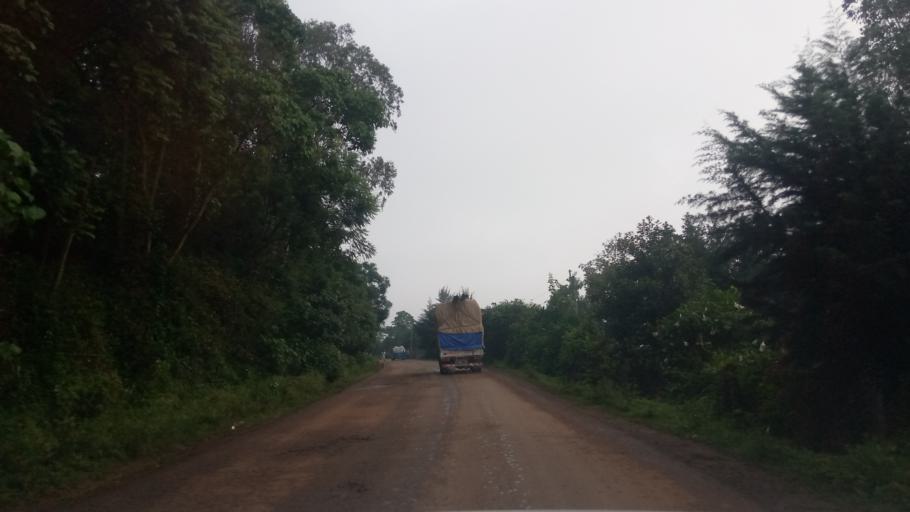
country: ET
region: Oromiya
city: Jima
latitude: 7.6904
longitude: 36.8255
